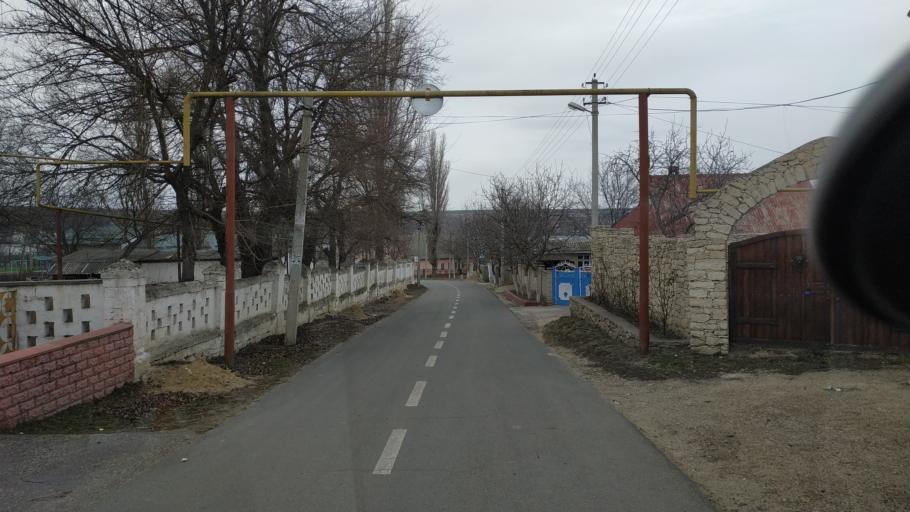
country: MD
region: Telenesti
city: Cocieri
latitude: 47.3474
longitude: 29.0910
